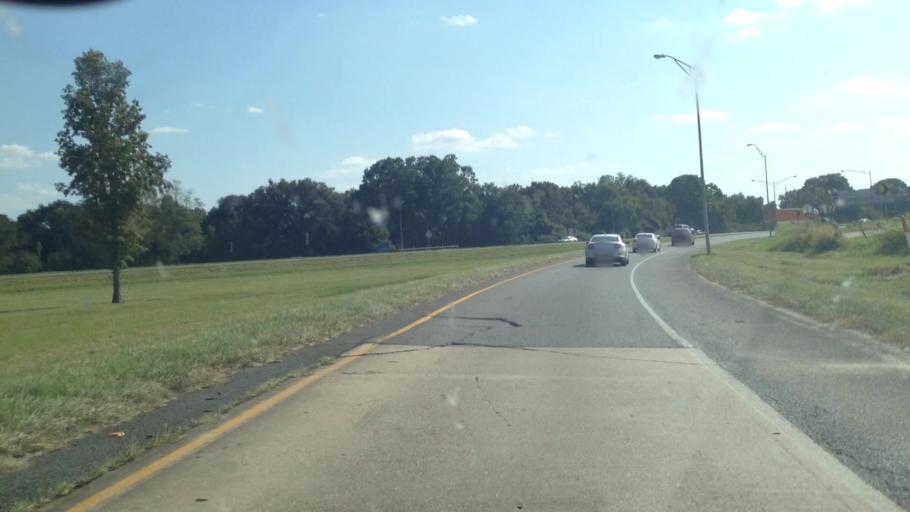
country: US
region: Louisiana
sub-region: Lafayette Parish
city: Lafayette
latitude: 30.2594
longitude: -92.0185
